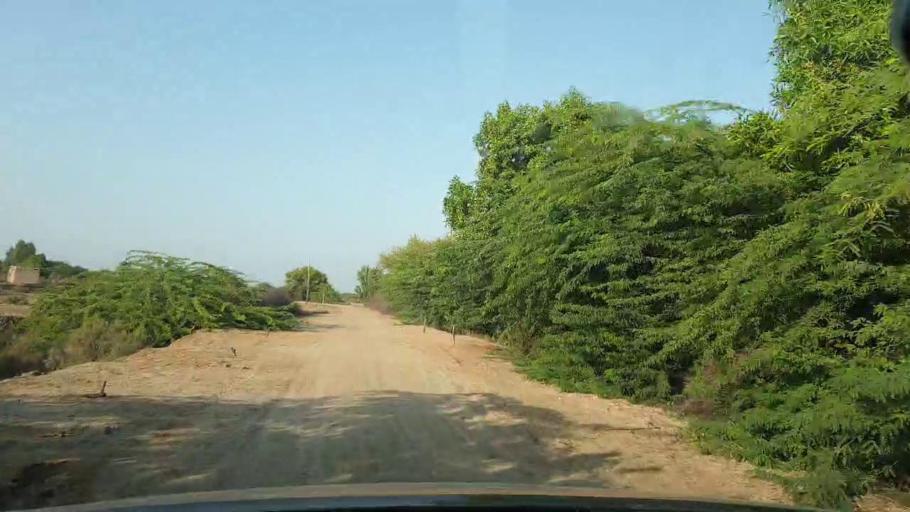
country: PK
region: Sindh
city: Naukot
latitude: 24.8112
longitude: 69.2038
